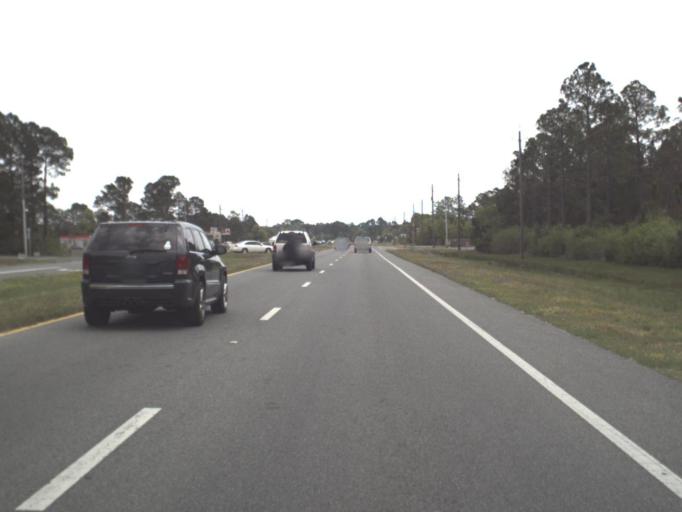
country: US
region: Florida
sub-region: Escambia County
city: Myrtle Grove
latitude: 30.3993
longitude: -87.3109
